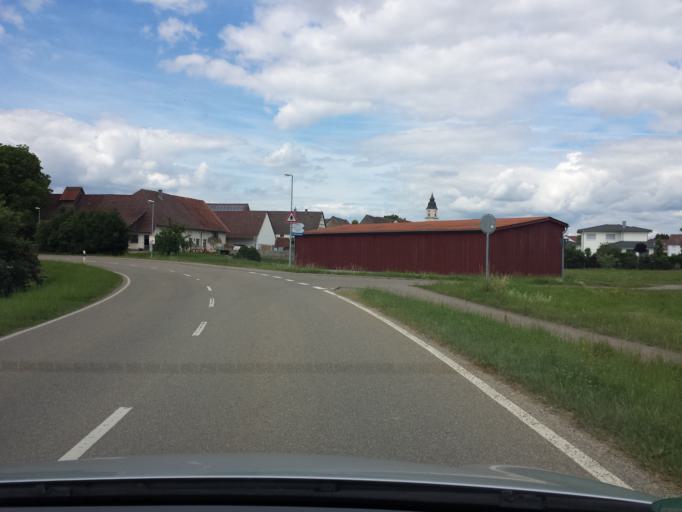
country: DE
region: Baden-Wuerttemberg
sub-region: Tuebingen Region
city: Achstetten
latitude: 48.2587
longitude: 9.9212
